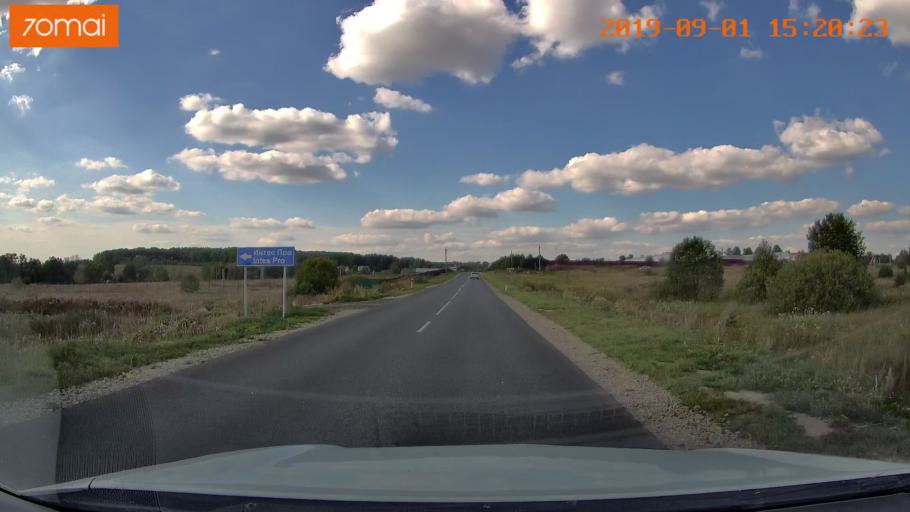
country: RU
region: Kaluga
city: Maloyaroslavets
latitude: 54.9190
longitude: 36.4805
